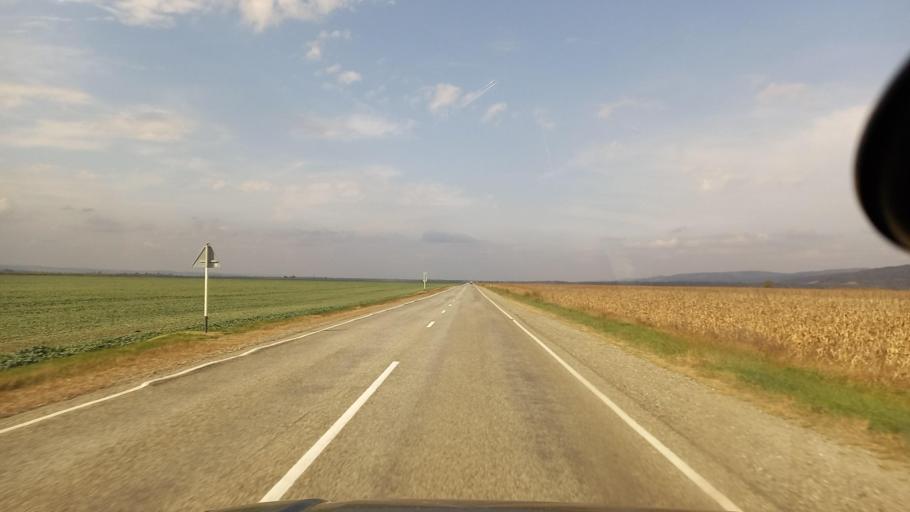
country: RU
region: Krasnodarskiy
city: Perepravnaya
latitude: 44.3017
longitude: 40.8610
